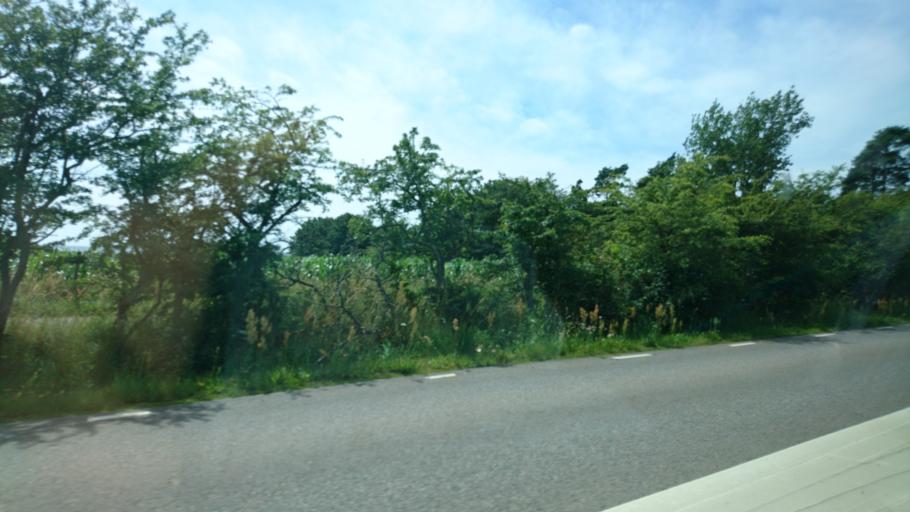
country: SE
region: Skane
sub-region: Skurups Kommun
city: Skivarp
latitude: 55.3873
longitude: 13.5105
